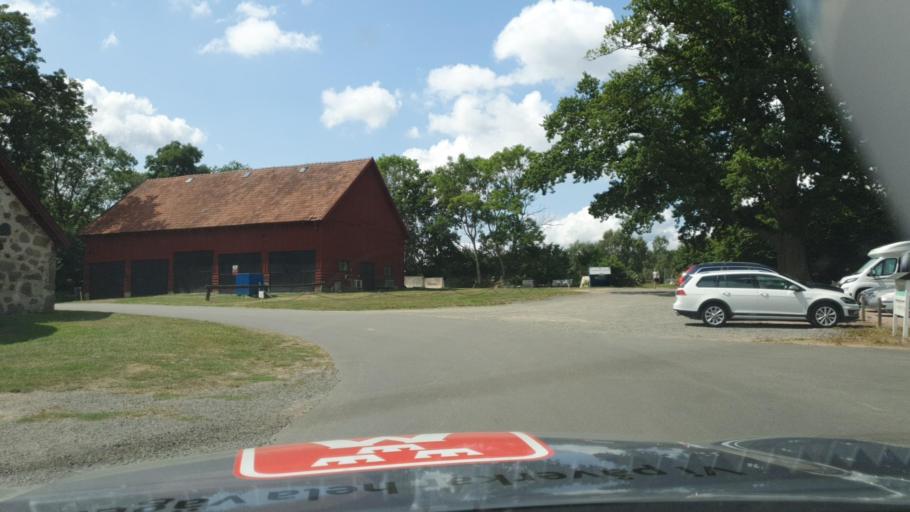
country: SE
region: Skane
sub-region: Kristianstads Kommun
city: Onnestad
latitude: 56.0133
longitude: 14.0493
